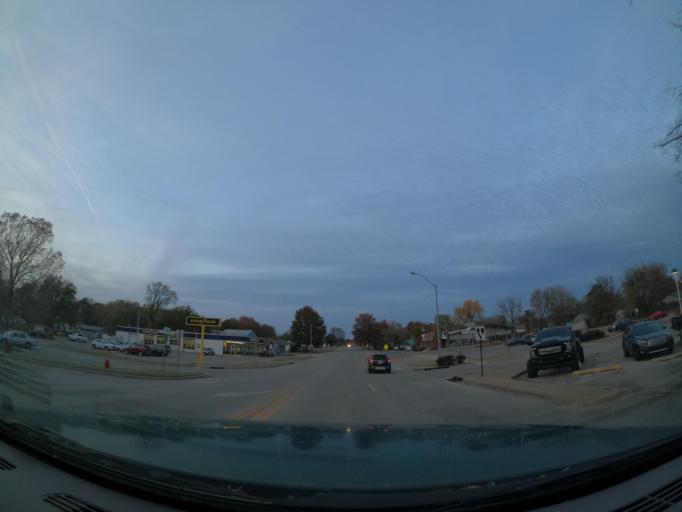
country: US
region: Oklahoma
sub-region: Tulsa County
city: Broken Arrow
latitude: 36.0561
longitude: -95.7908
